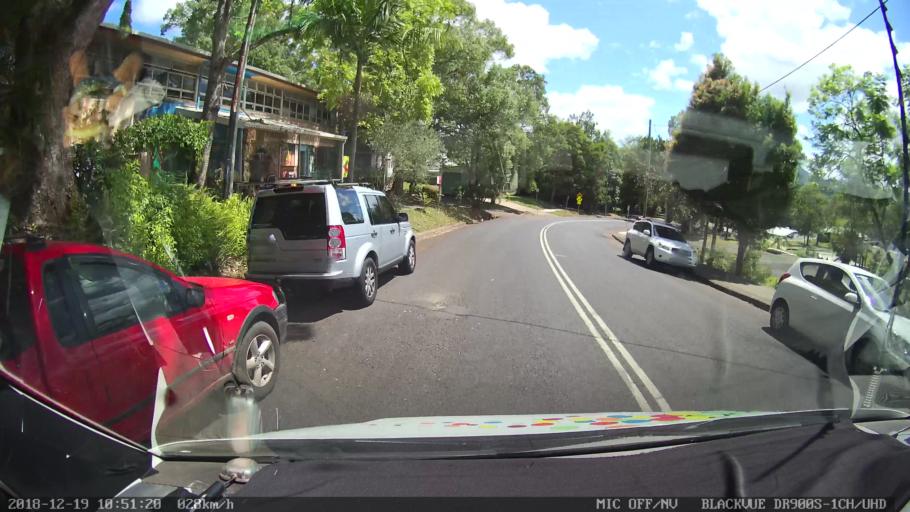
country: AU
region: New South Wales
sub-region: Lismore Municipality
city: Nimbin
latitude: -28.5950
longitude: 153.2232
